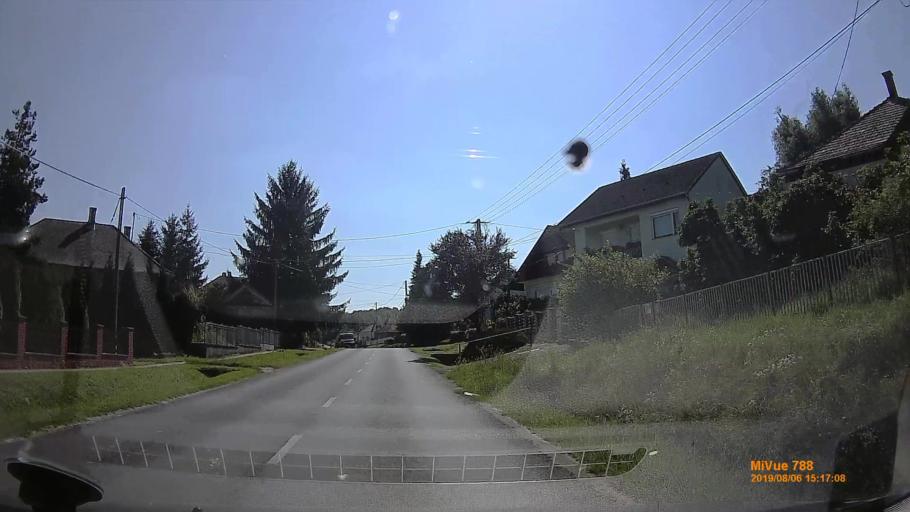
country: HU
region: Zala
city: Murakeresztur
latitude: 46.3172
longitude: 16.9665
